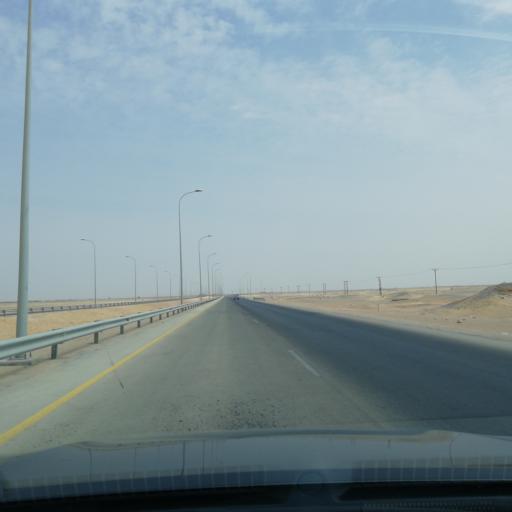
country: OM
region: Zufar
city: Salalah
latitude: 17.6769
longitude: 54.0555
